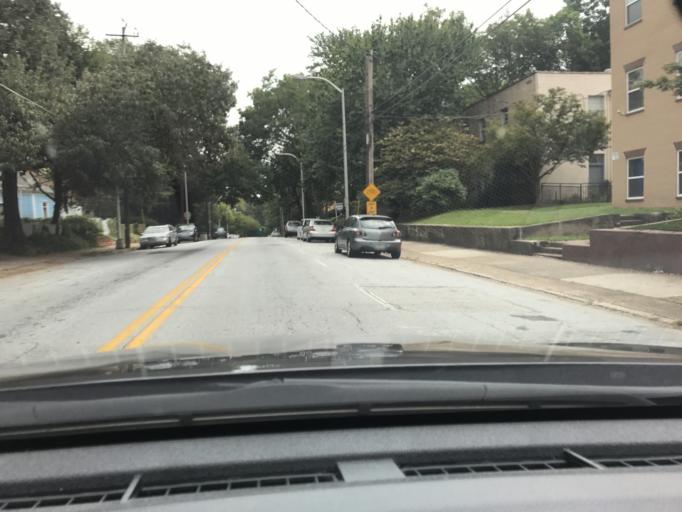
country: US
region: Georgia
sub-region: Fulton County
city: Atlanta
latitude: 33.7367
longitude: -84.3763
